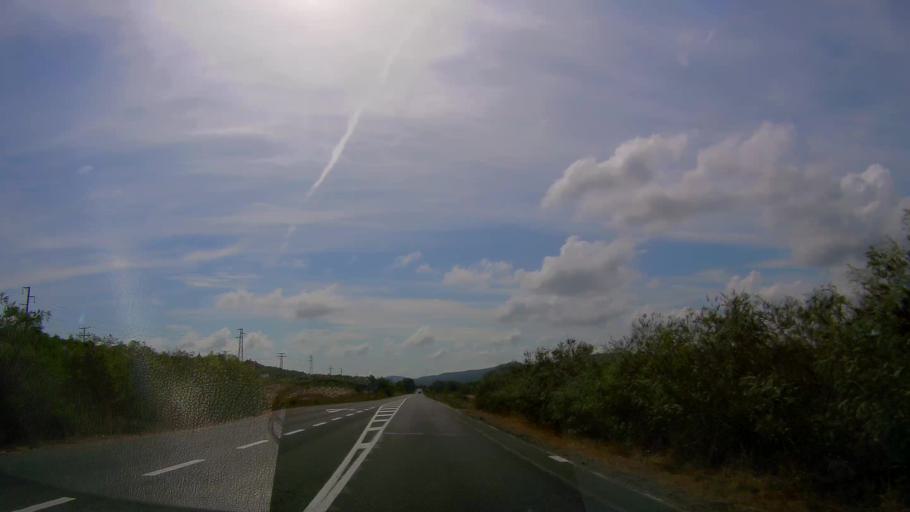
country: BG
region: Burgas
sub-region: Obshtina Sozopol
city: Sozopol
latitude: 42.3774
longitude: 27.6820
